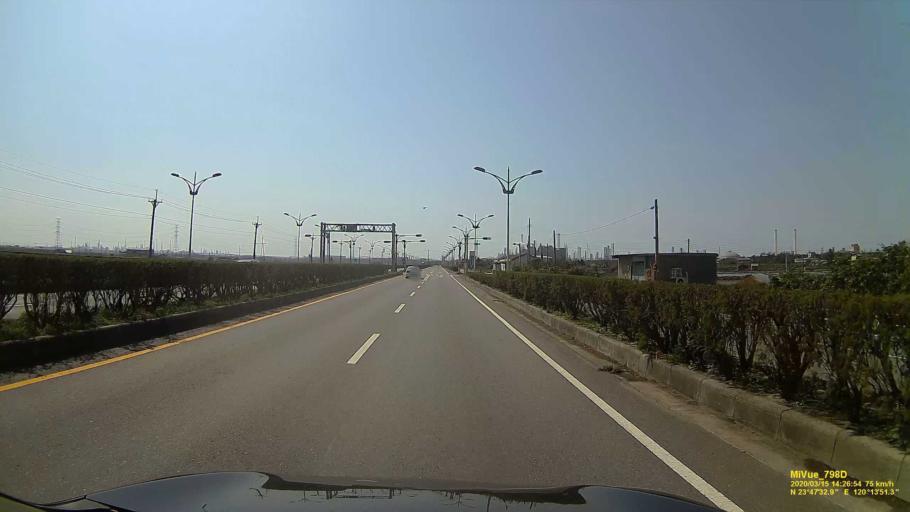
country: TW
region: Taiwan
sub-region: Yunlin
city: Douliu
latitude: 23.7925
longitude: 120.2305
